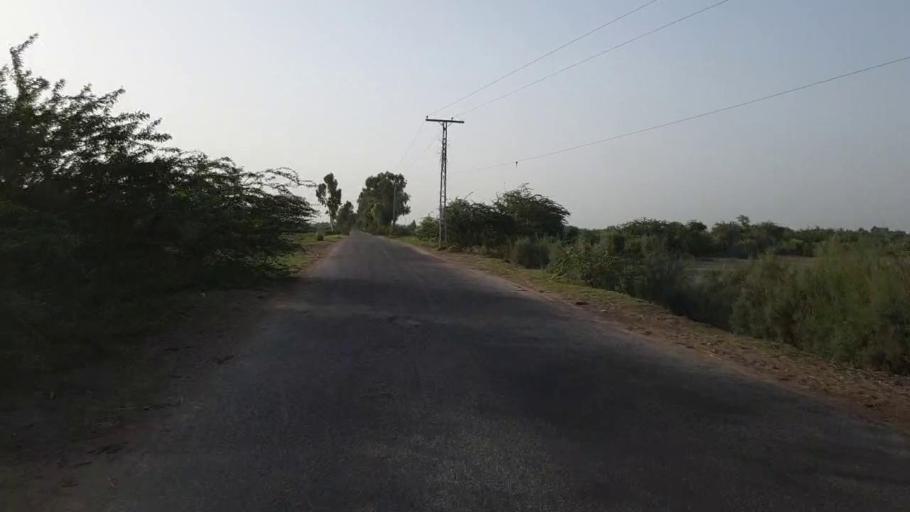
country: PK
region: Sindh
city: Bozdar
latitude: 27.1040
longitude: 68.9622
